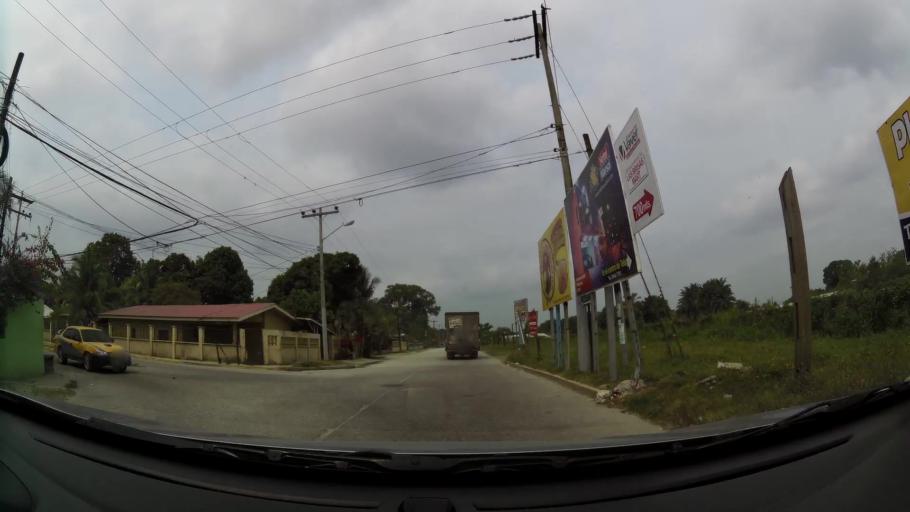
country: HN
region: Atlantida
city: Tela
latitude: 15.7714
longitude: -87.4821
